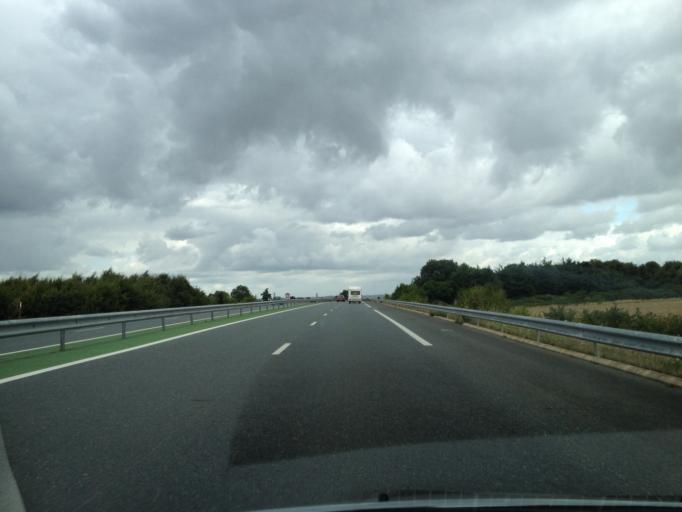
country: FR
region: Pays de la Loire
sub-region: Departement de la Vendee
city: Saint-Laurent-sur-Sevre
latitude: 46.9786
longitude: -0.9175
